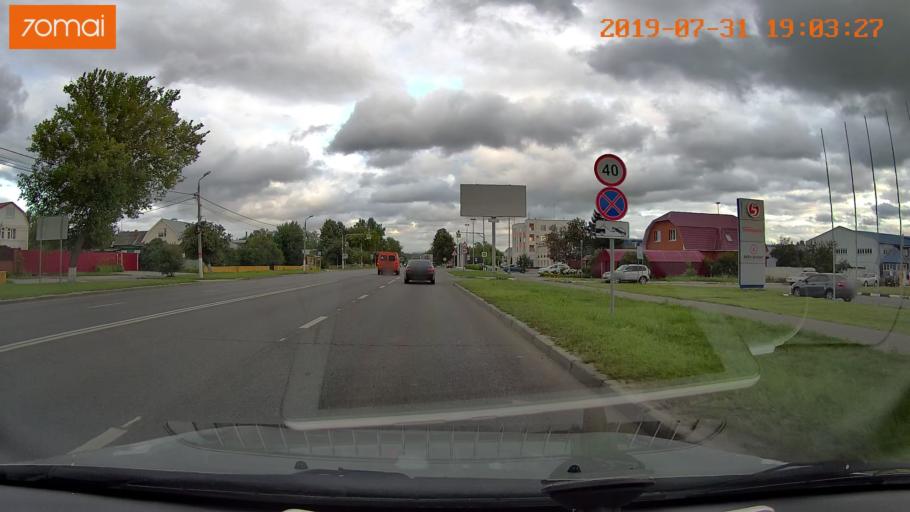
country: RU
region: Moskovskaya
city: Raduzhnyy
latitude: 55.1145
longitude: 38.7374
